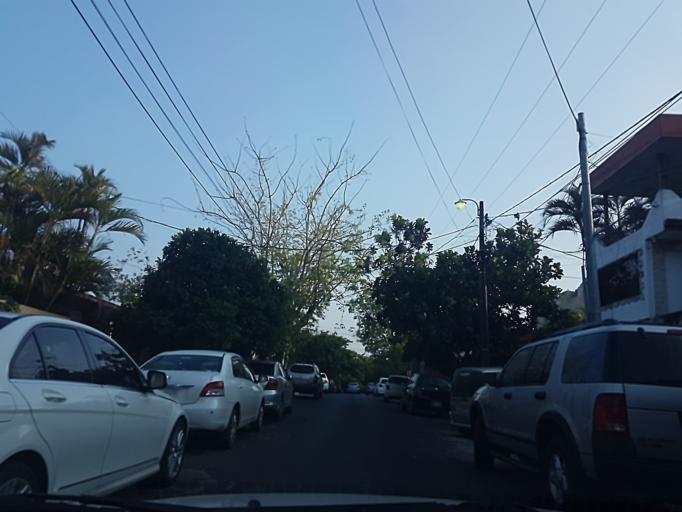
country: PY
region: Presidente Hayes
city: Nanawa
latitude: -25.2868
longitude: -57.6575
